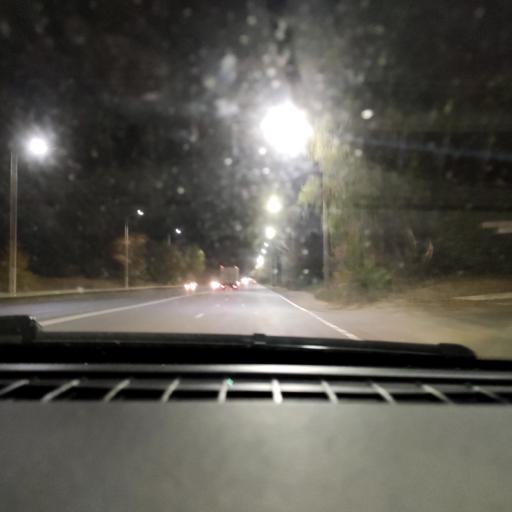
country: RU
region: Voronezj
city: Maslovka
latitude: 51.6274
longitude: 39.2852
